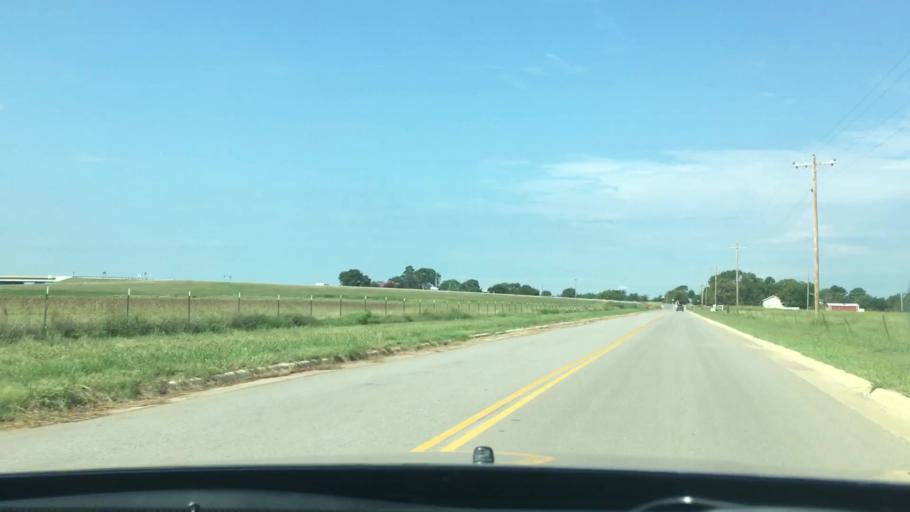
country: US
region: Oklahoma
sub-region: Bryan County
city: Durant
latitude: 33.9684
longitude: -96.3682
